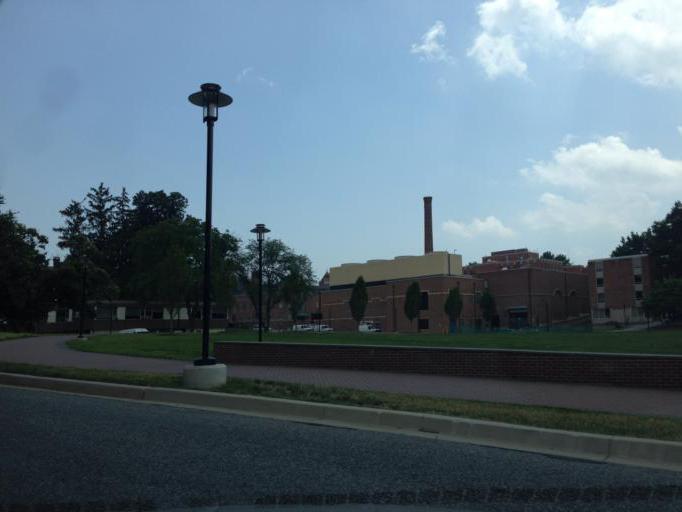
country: US
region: Maryland
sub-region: Baltimore County
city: Towson
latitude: 39.3956
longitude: -76.6076
